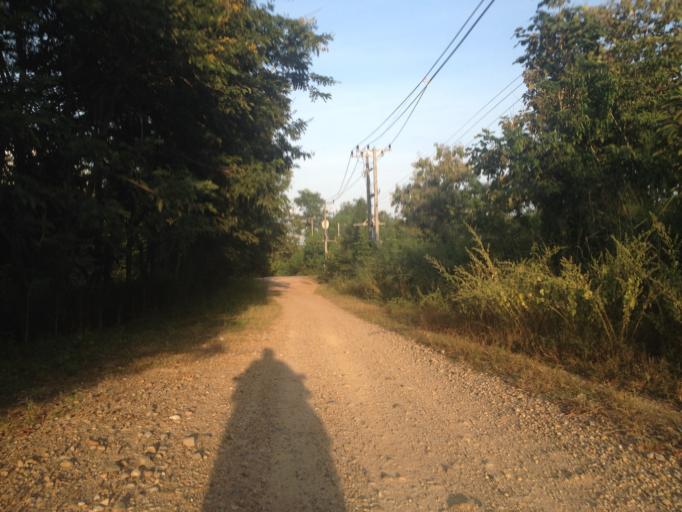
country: TH
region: Chiang Mai
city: Chiang Mai
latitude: 18.7650
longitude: 98.9338
